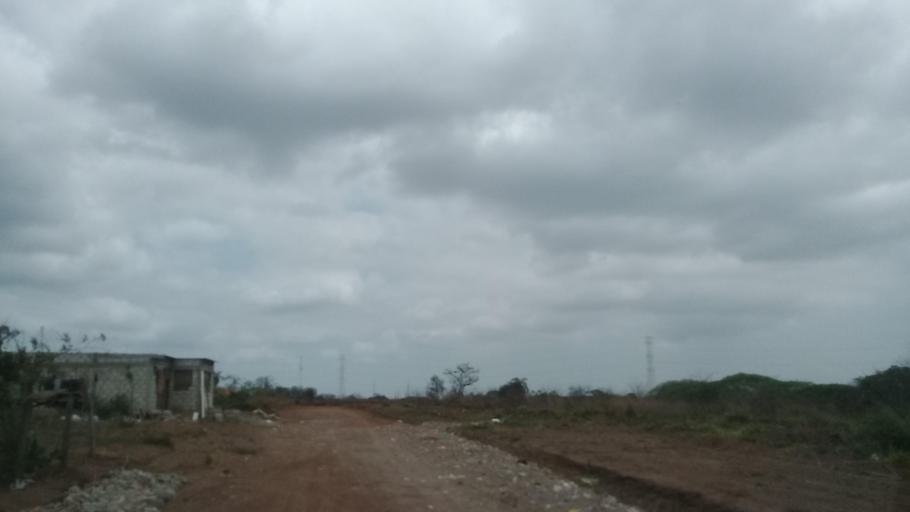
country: MX
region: Veracruz
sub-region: Veracruz
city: Las Amapolas
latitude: 19.1363
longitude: -96.2418
